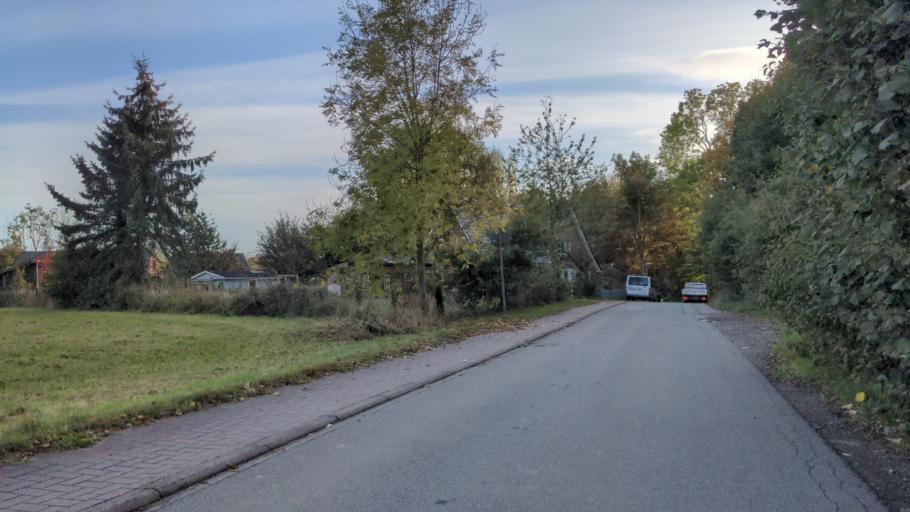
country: DE
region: Schleswig-Holstein
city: Manhagen
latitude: 54.1883
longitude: 10.9418
